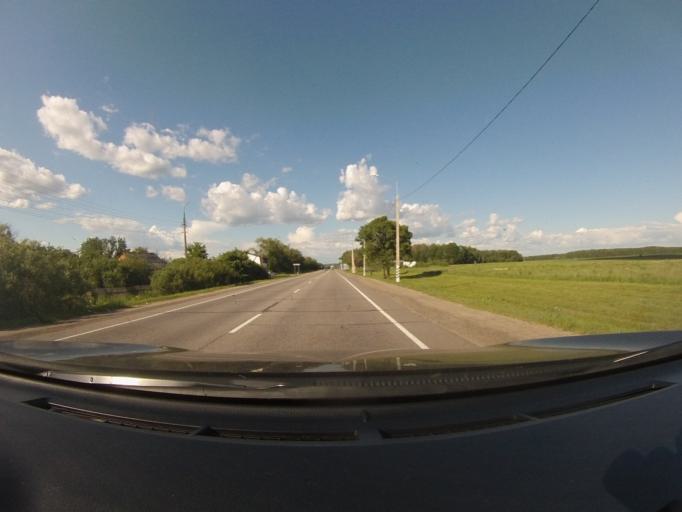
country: RU
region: Tula
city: Bol'shoye Skuratovo
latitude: 53.4000
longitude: 36.7630
